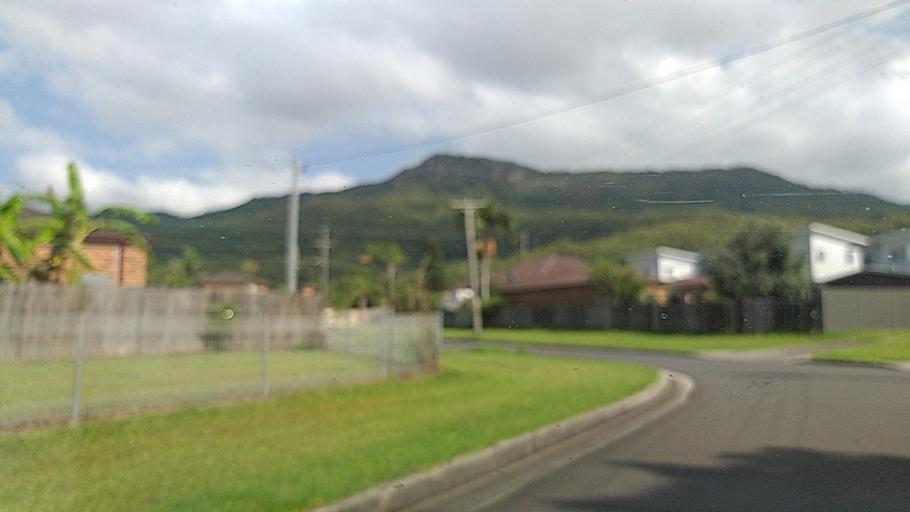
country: AU
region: New South Wales
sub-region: Wollongong
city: Corrimal
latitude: -34.3758
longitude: 150.8902
